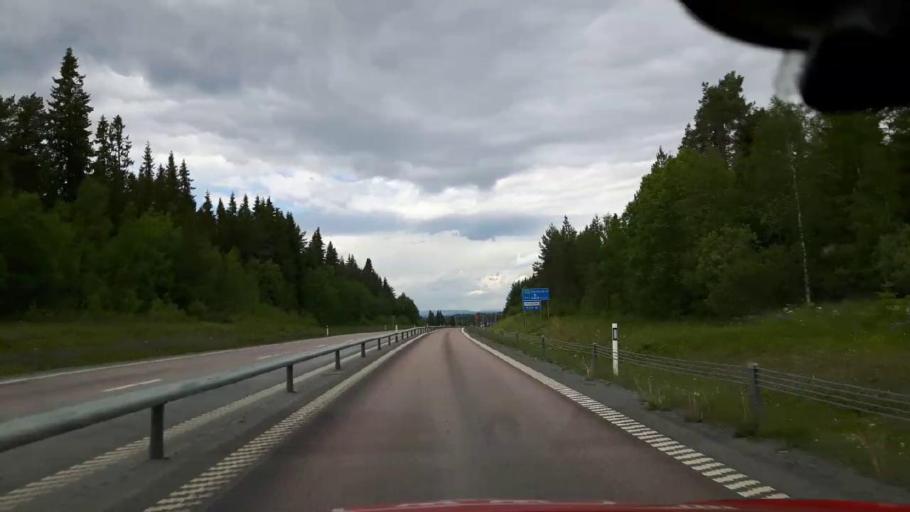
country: SE
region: Jaemtland
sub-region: Krokoms Kommun
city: Krokom
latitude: 63.2637
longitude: 14.5443
